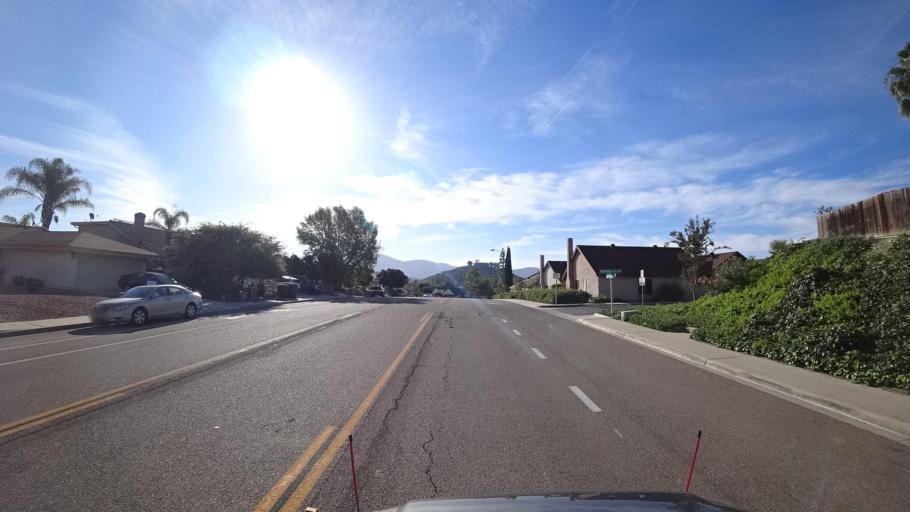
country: US
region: California
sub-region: San Diego County
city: Spring Valley
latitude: 32.7338
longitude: -116.9830
